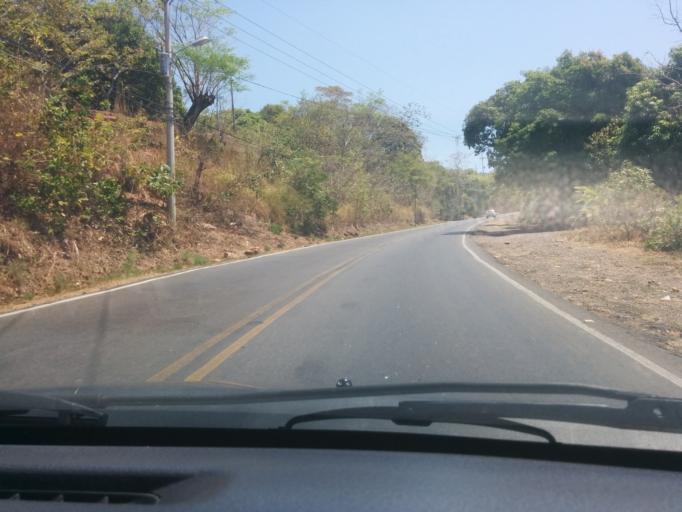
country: CR
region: Puntarenas
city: Esparza
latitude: 10.0146
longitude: -84.6167
